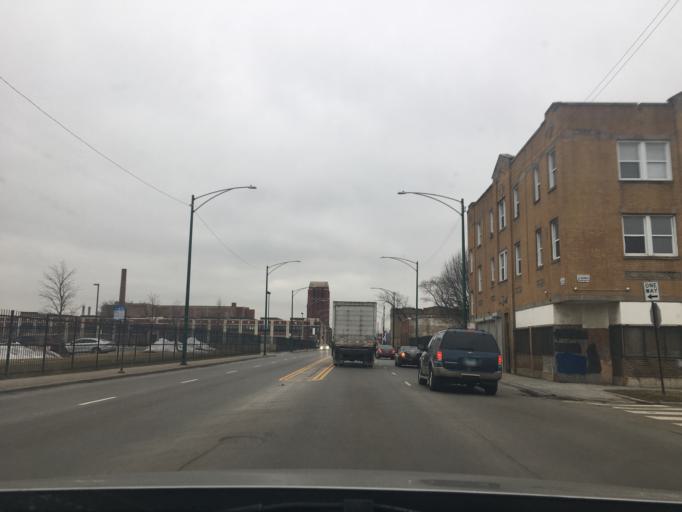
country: US
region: Illinois
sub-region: Cook County
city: Oak Park
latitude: 41.9042
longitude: -87.7460
